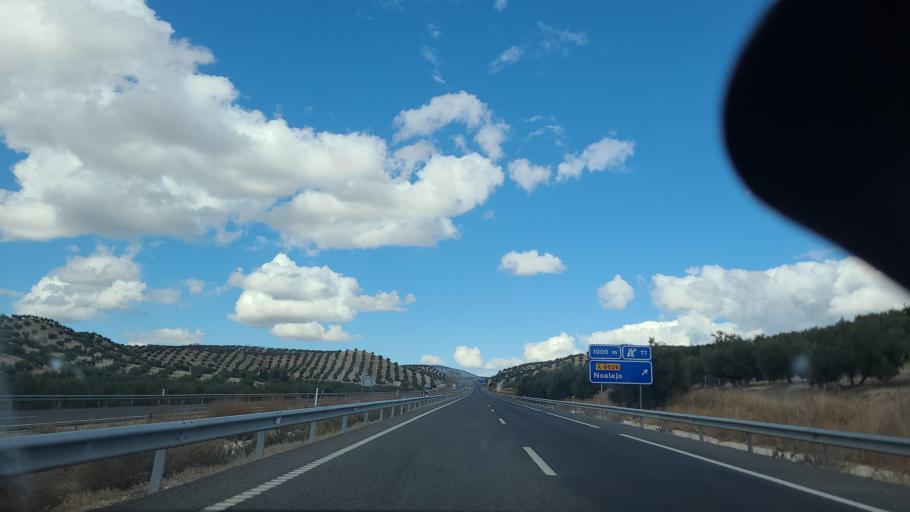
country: ES
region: Andalusia
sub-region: Provincia de Jaen
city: Noalejo
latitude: 37.5179
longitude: -3.6378
